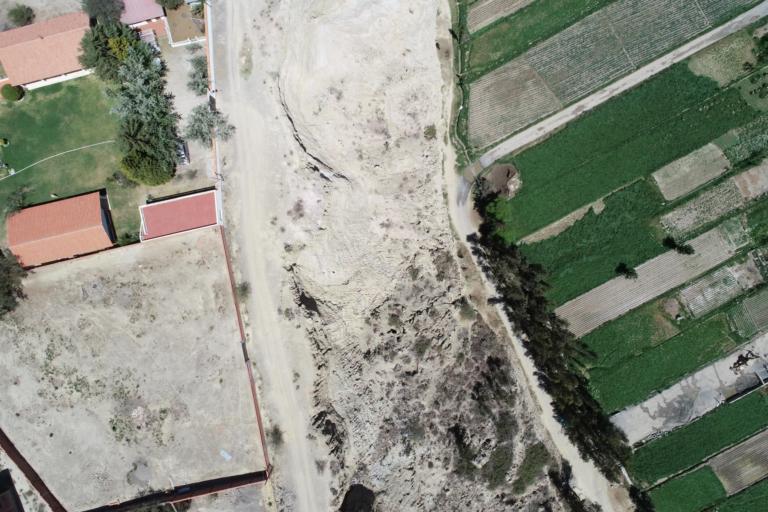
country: BO
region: La Paz
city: La Paz
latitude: -16.6474
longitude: -68.0451
